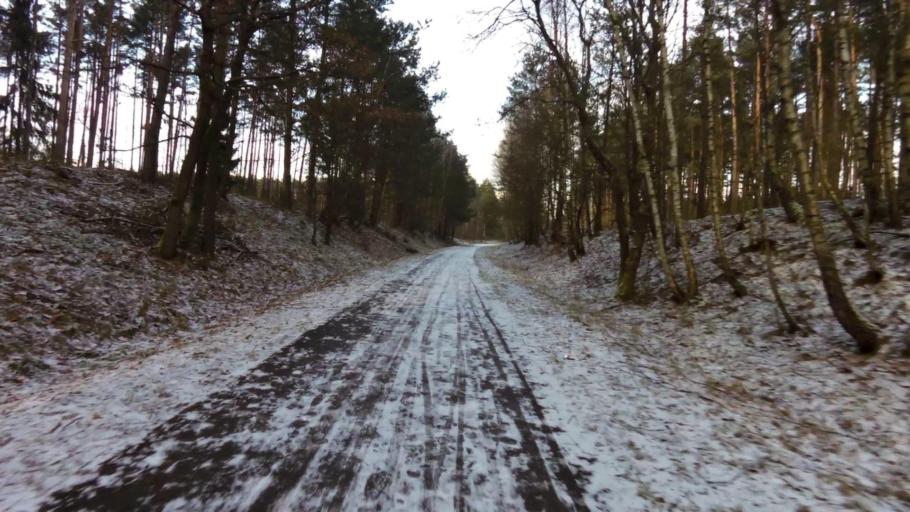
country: PL
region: West Pomeranian Voivodeship
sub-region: Powiat drawski
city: Zlocieniec
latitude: 53.5518
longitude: 16.0209
